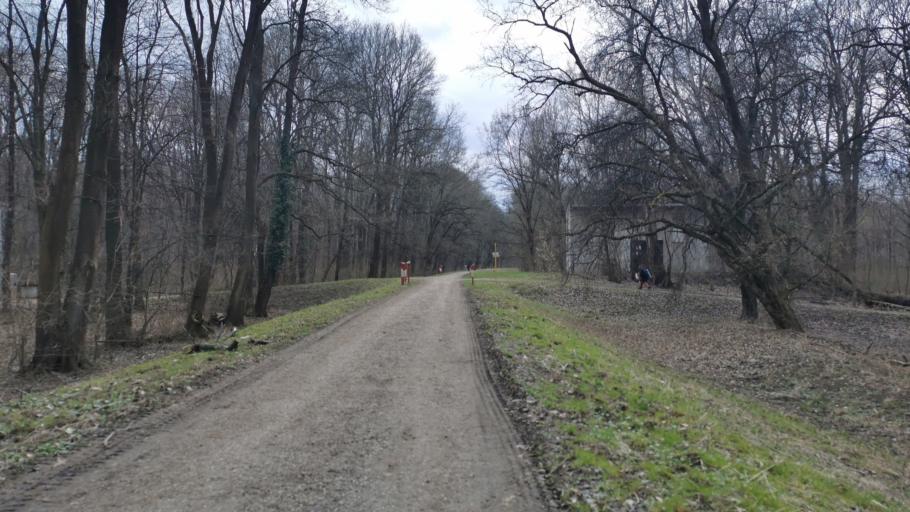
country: CZ
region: South Moravian
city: Rohatec
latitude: 48.8579
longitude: 17.1812
